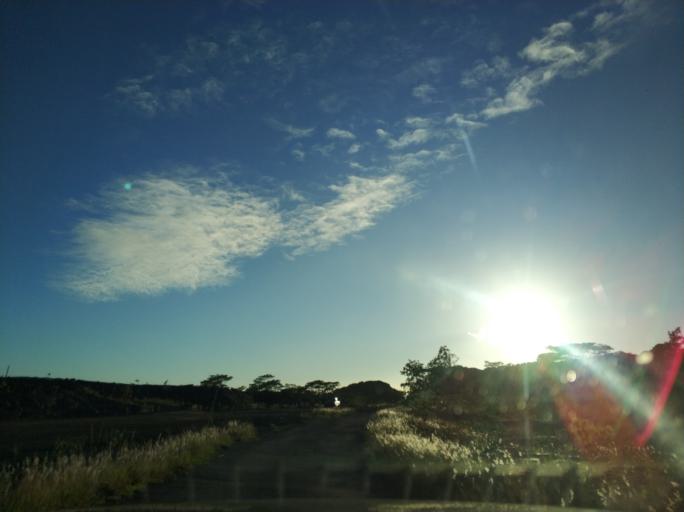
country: US
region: Hawaii
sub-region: Hawaii County
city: Leilani Estates
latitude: 19.3603
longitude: -154.9797
